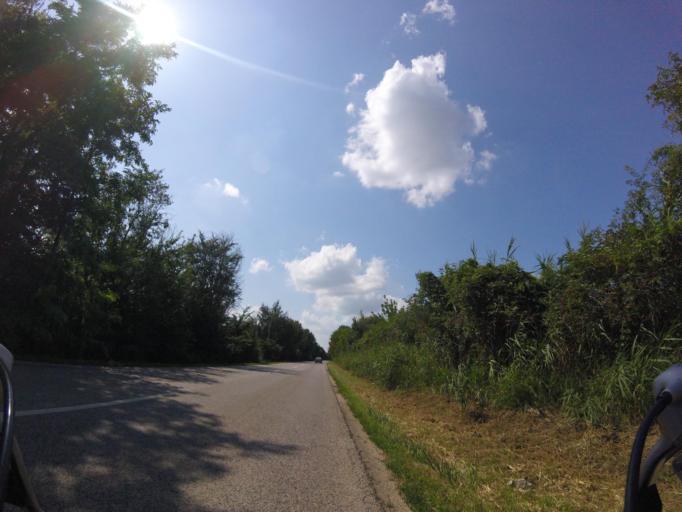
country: HU
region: Fejer
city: Etyek
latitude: 47.4830
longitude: 18.7744
